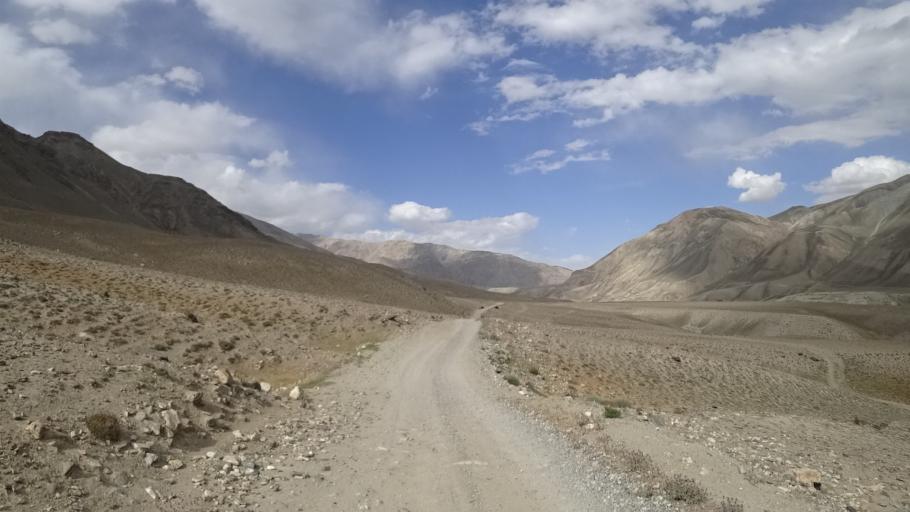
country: AF
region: Badakhshan
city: Khandud
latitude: 37.1909
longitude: 72.7621
